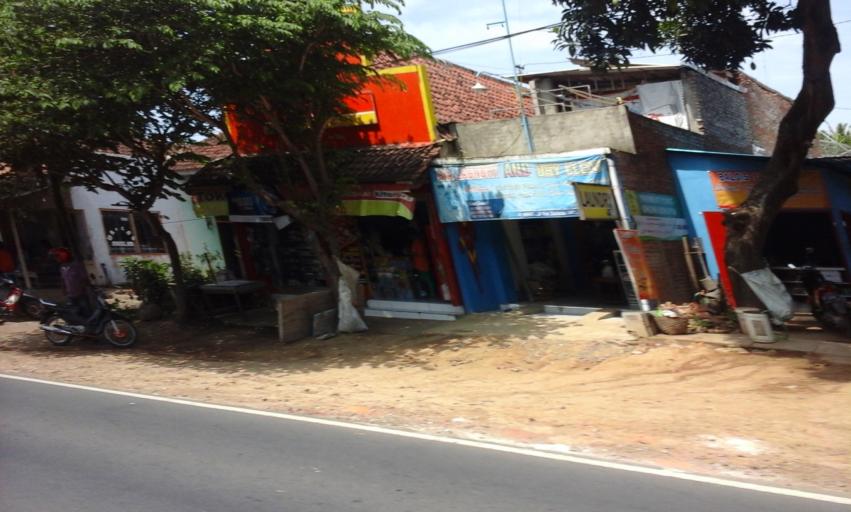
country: ID
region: East Java
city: Klatakan
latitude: -8.1756
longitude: 114.3838
